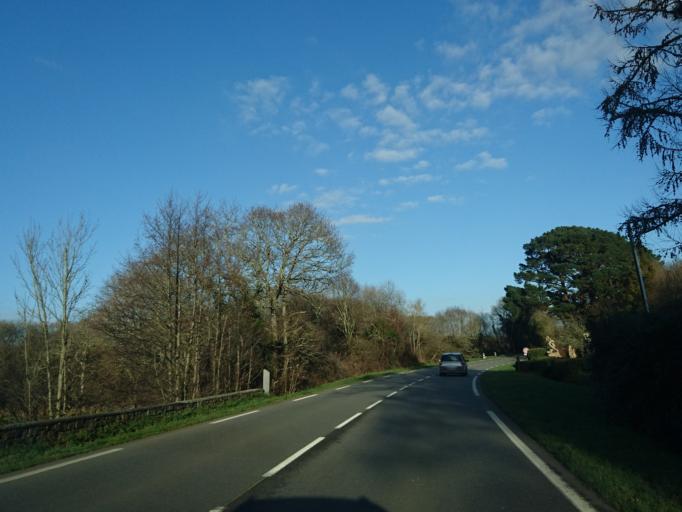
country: FR
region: Brittany
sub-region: Departement du Finistere
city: Le Faou
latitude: 48.2914
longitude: -4.1975
